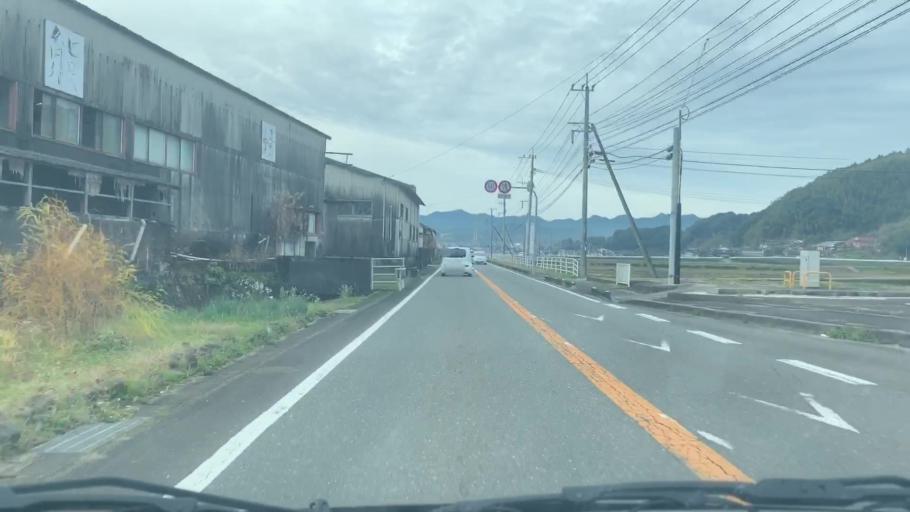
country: JP
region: Saga Prefecture
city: Ureshinomachi-shimojuku
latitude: 33.1351
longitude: 130.0150
